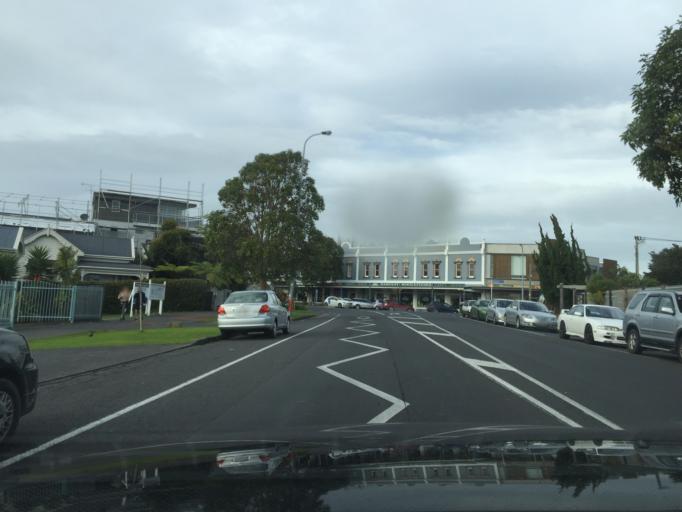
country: NZ
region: Auckland
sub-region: Auckland
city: Auckland
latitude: -36.8579
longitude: 174.7304
